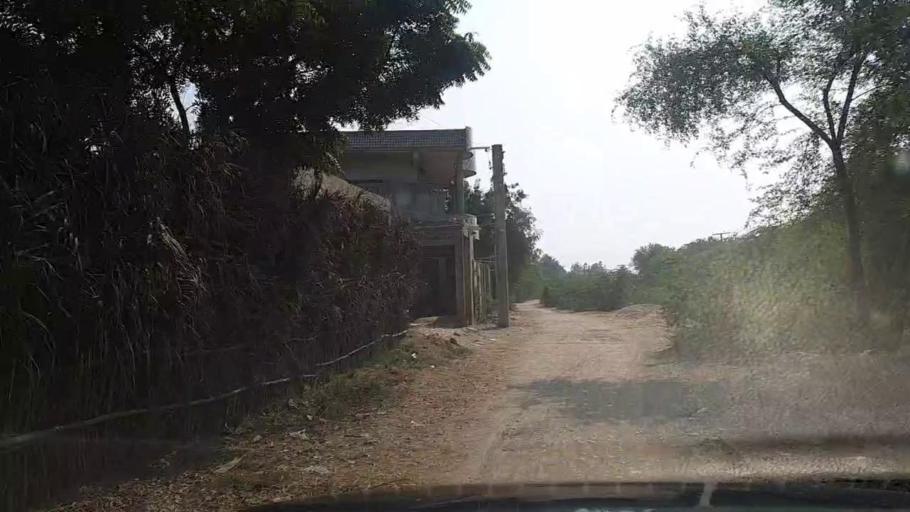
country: PK
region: Sindh
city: Mirpur Batoro
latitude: 24.6976
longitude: 68.2191
